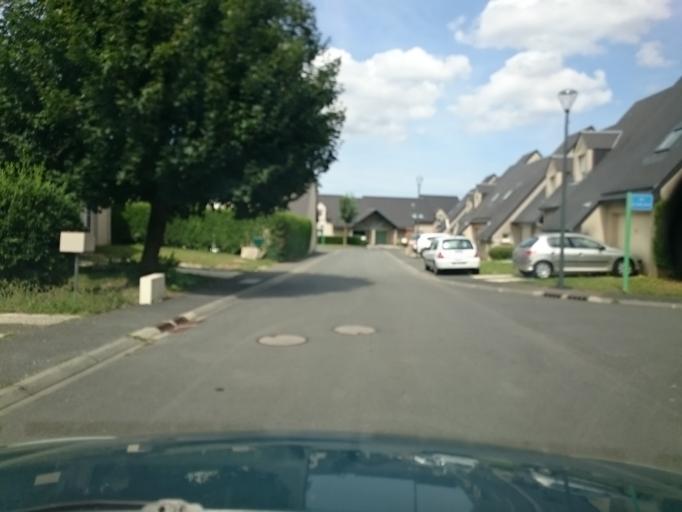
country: FR
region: Lower Normandy
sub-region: Departement du Calvados
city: Ifs
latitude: 49.1378
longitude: -0.3477
